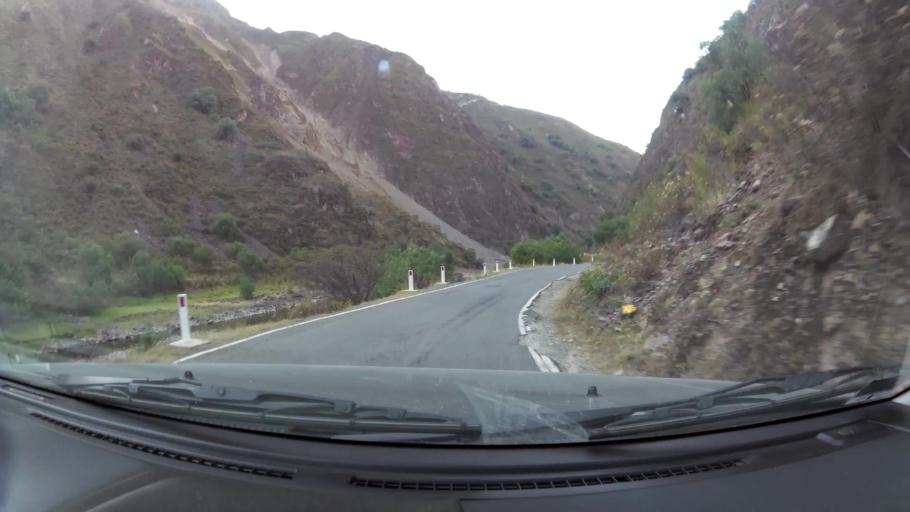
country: PE
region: Huancavelica
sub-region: Provincia de Churcampa
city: La Esmeralda
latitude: -12.5530
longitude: -74.7079
